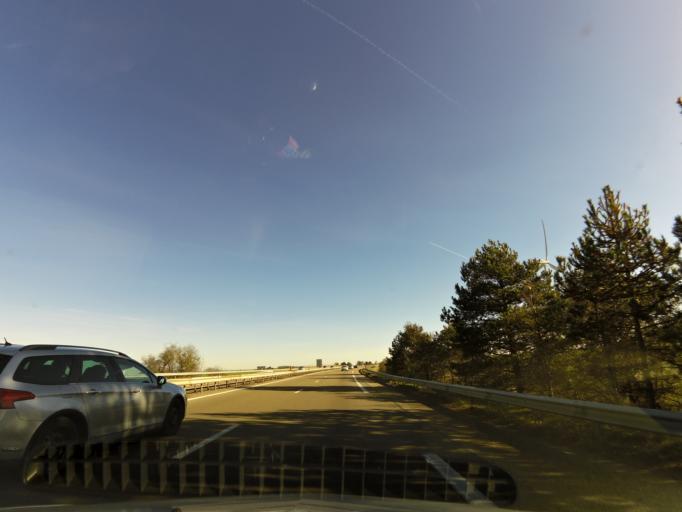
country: FR
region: Bourgogne
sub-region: Departement de l'Yonne
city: Saint-Bris-le-Vineux
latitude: 47.7764
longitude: 3.7032
